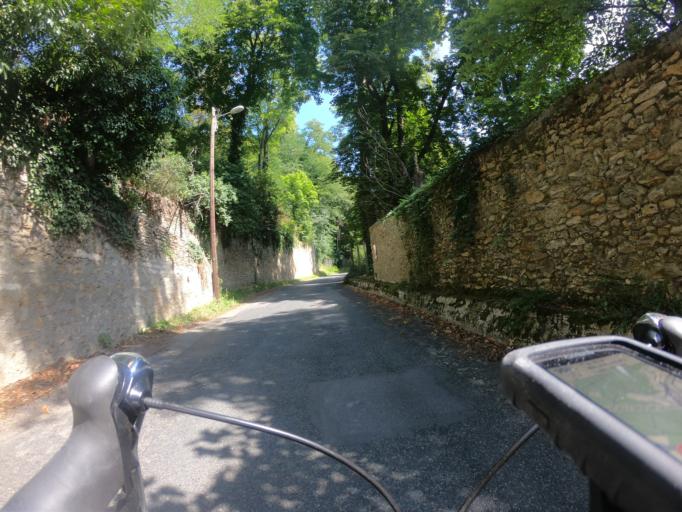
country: FR
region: Ile-de-France
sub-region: Departement des Yvelines
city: Jouy-en-Josas
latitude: 48.7657
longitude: 2.1749
